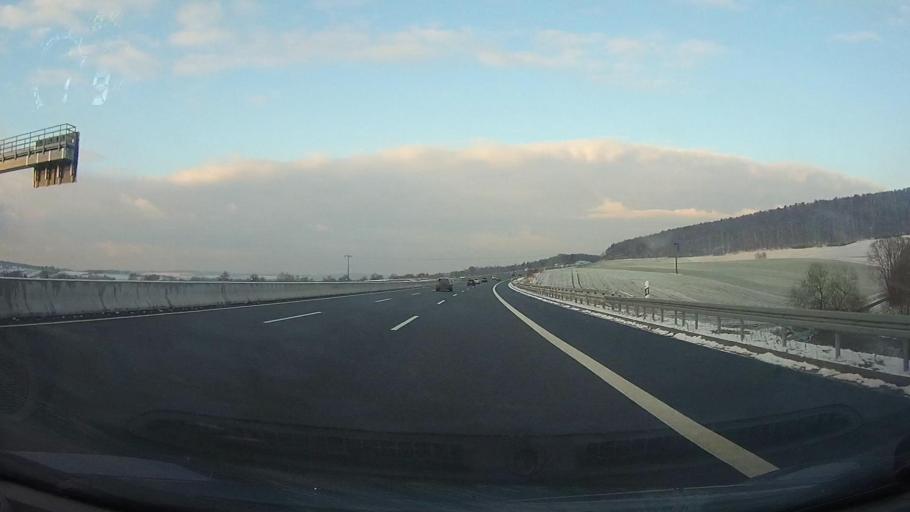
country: DE
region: Lower Saxony
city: Bockenem
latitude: 51.9579
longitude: 10.1401
